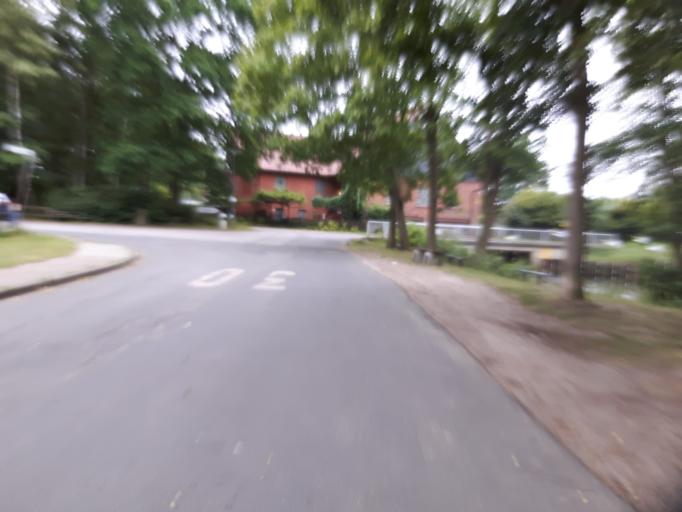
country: DE
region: Lower Saxony
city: Winsen
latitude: 53.3261
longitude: 10.1971
